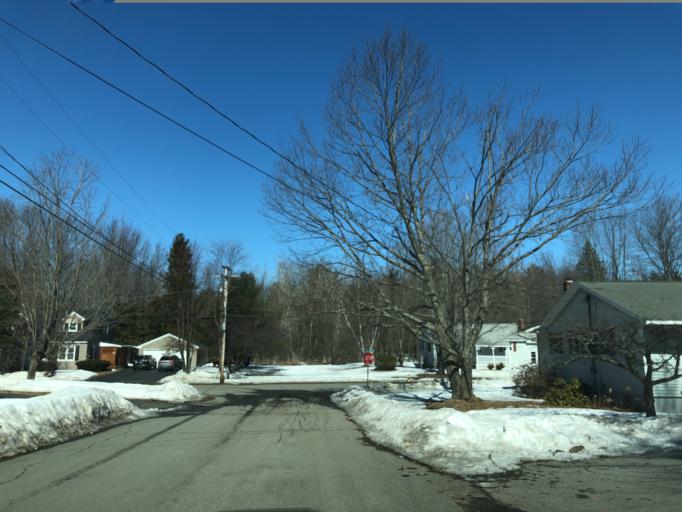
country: US
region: Maine
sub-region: Penobscot County
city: Brewer
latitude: 44.8208
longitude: -68.7557
